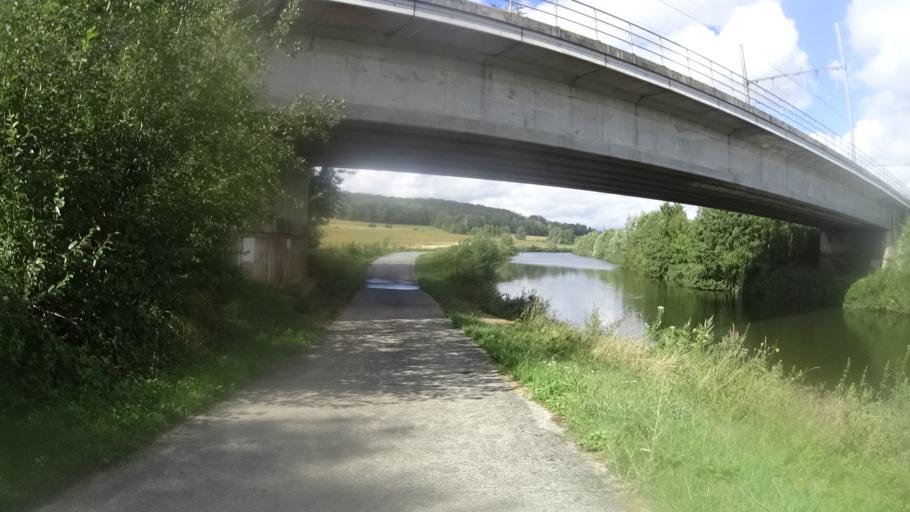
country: BE
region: Wallonia
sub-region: Province du Hainaut
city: Merbes-le-Chateau
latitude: 50.3187
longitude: 4.2030
